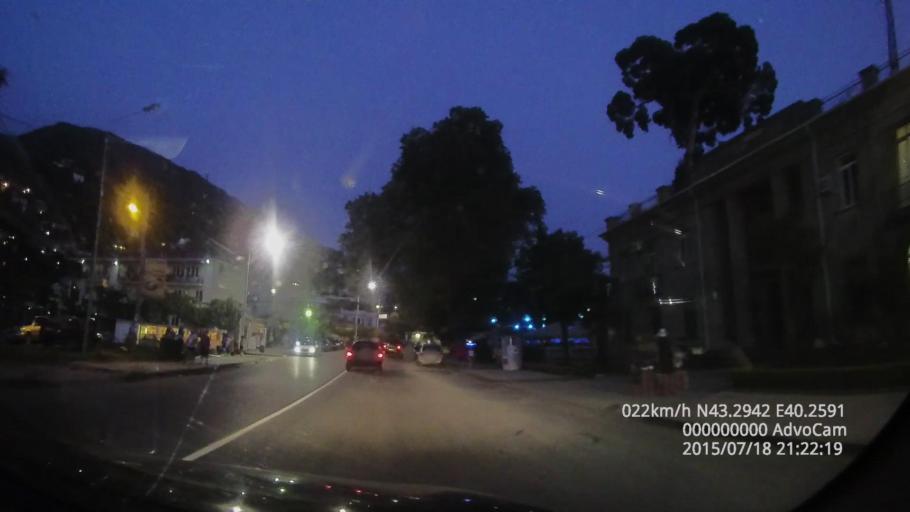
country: GE
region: Abkhazia
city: Gagra
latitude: 43.2941
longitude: 40.2593
